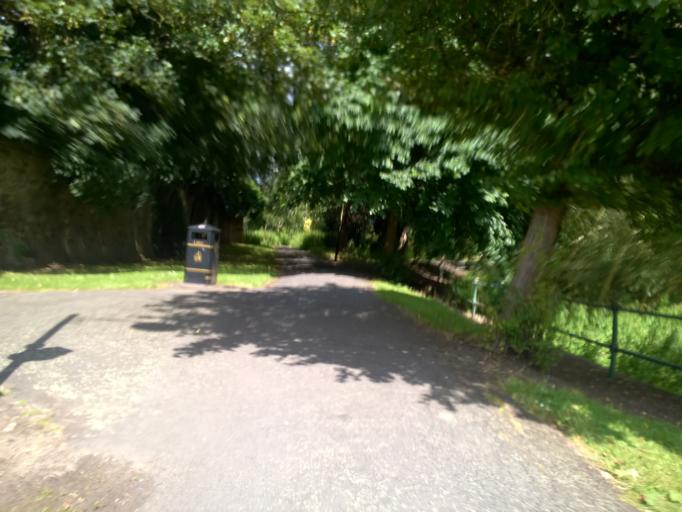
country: GB
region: England
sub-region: City of Leicester
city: Leicester
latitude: 52.6486
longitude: -1.1356
